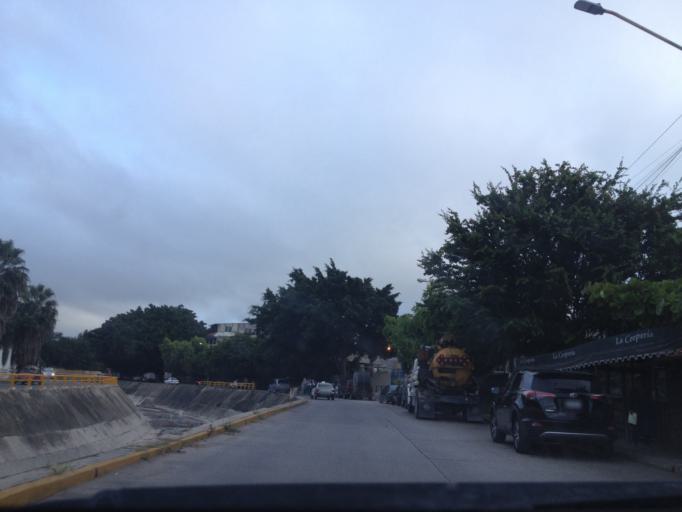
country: MX
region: Guerrero
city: Chilpancingo de los Bravos
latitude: 17.5444
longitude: -99.5017
